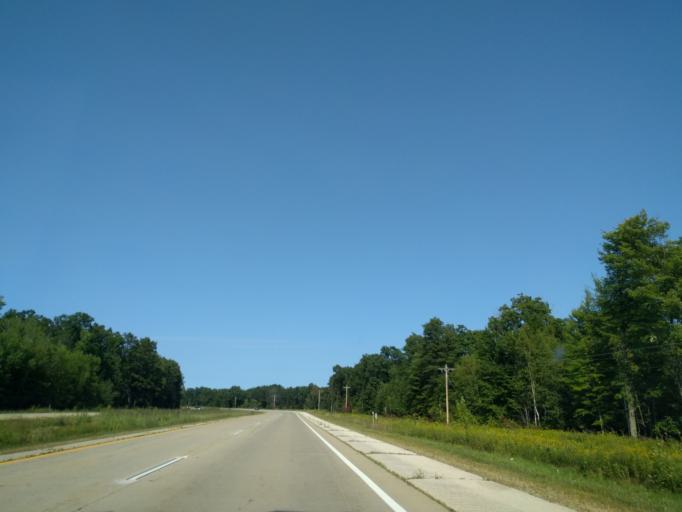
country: US
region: Wisconsin
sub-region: Oconto County
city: Oconto
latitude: 44.8492
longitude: -87.9026
